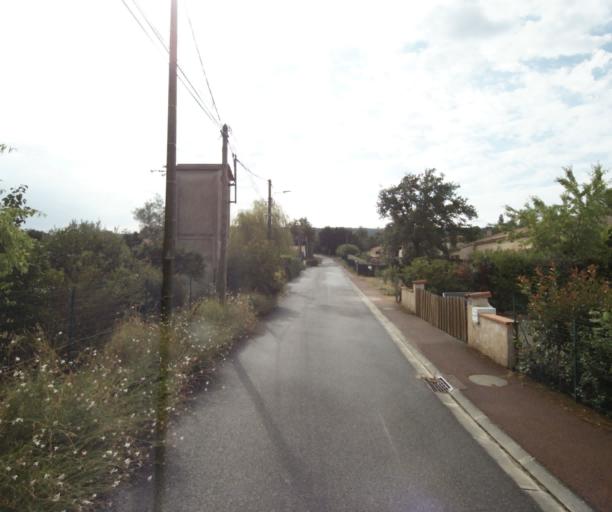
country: FR
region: Midi-Pyrenees
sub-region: Departement de la Haute-Garonne
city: Revel
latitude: 43.4259
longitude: 1.9825
